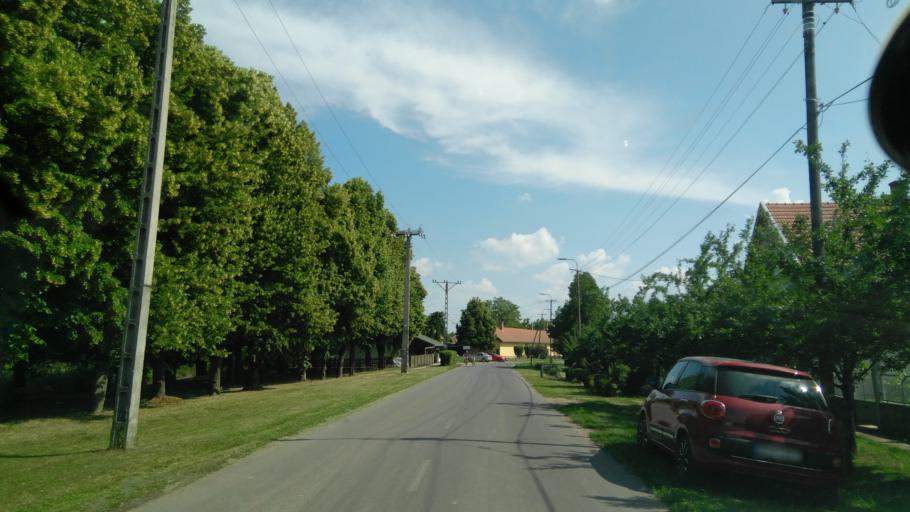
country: HU
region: Bekes
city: Doboz
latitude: 46.7296
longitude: 21.2408
